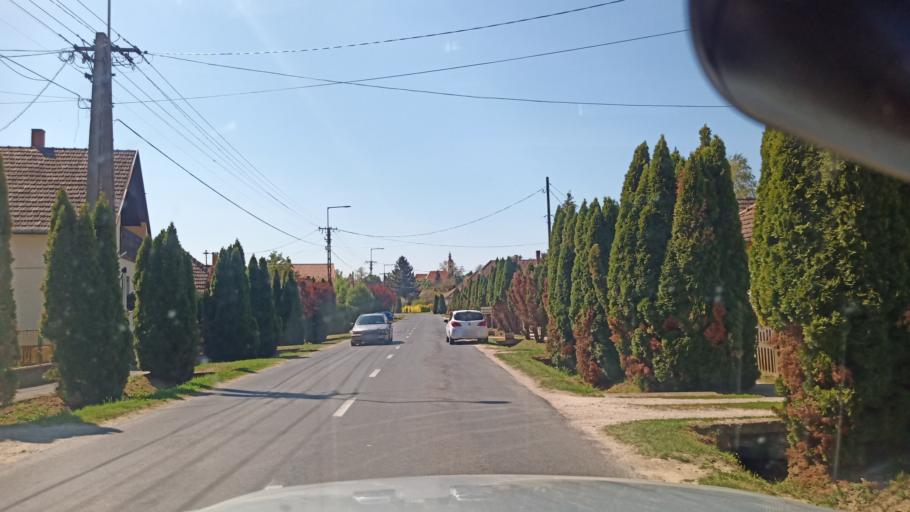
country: HU
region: Zala
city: Sarmellek
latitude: 46.7431
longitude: 17.1066
